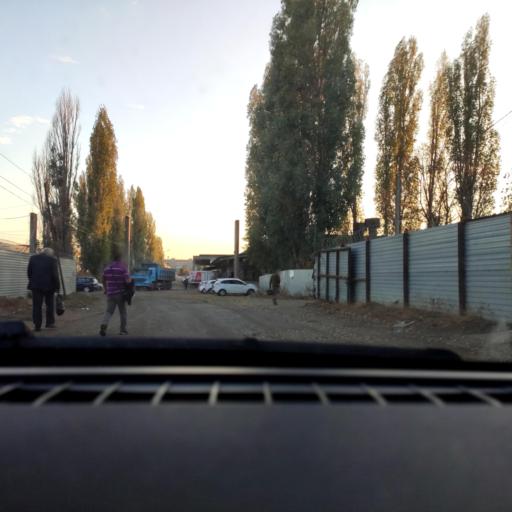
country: RU
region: Voronezj
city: Maslovka
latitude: 51.6399
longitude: 39.2844
